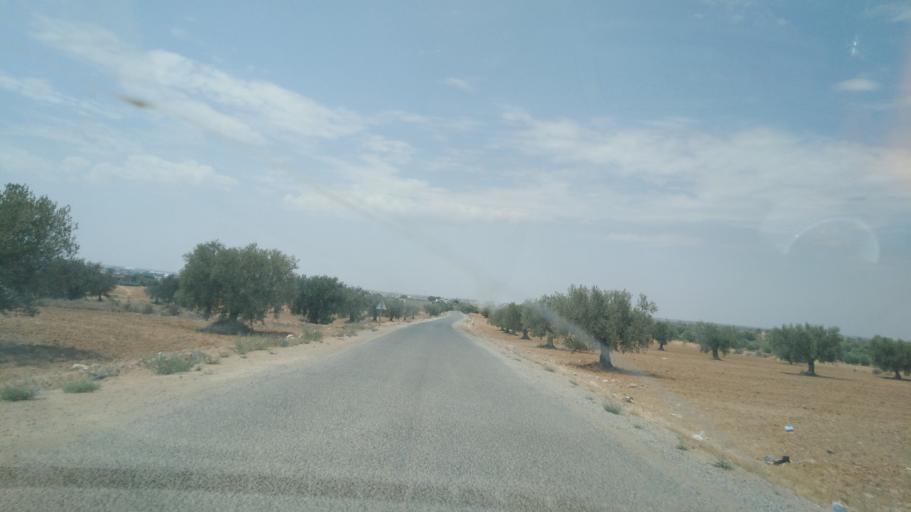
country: TN
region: Safaqis
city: Sfax
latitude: 34.7485
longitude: 10.5602
